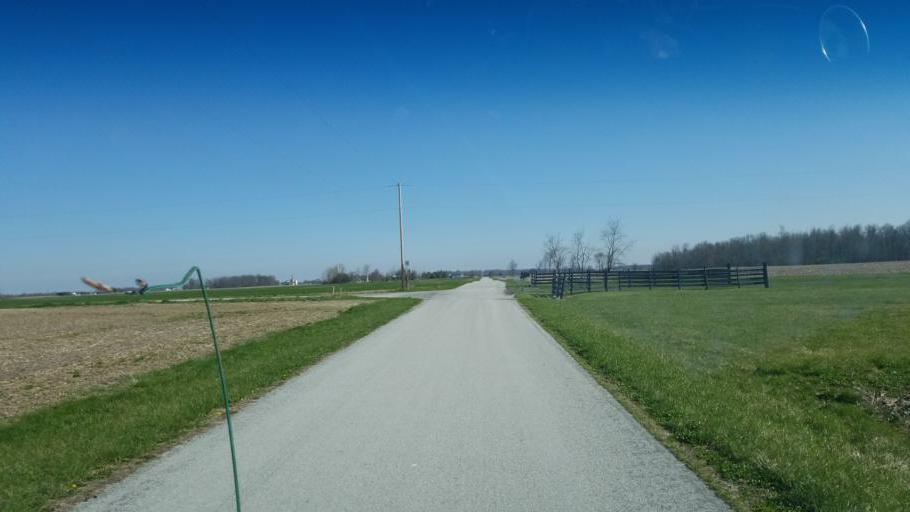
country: US
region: Ohio
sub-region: Hardin County
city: Kenton
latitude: 40.6873
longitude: -83.5593
